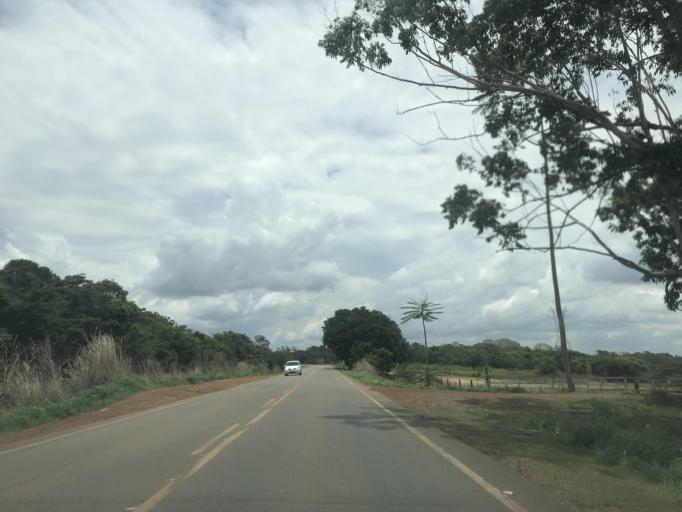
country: BR
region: Goias
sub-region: Vianopolis
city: Vianopolis
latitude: -16.7311
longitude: -48.4432
